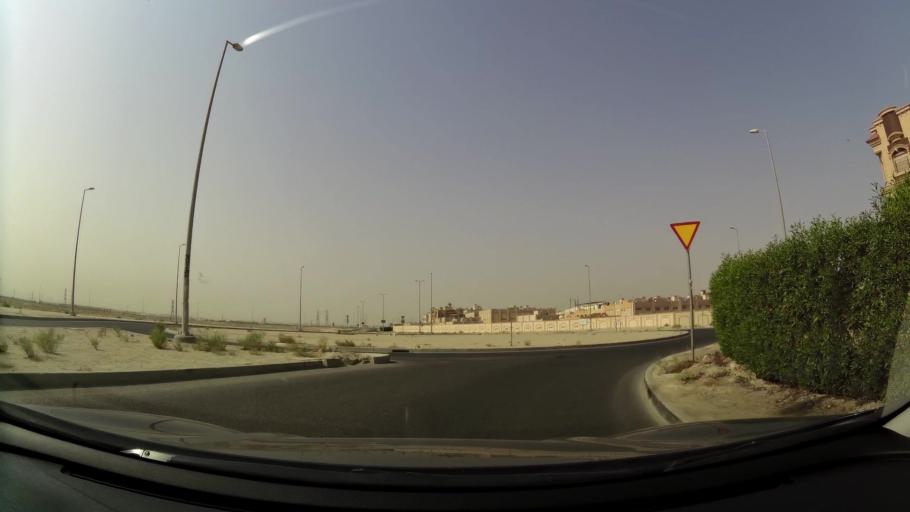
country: KW
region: Muhafazat al Jahra'
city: Al Jahra'
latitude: 29.3336
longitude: 47.7658
